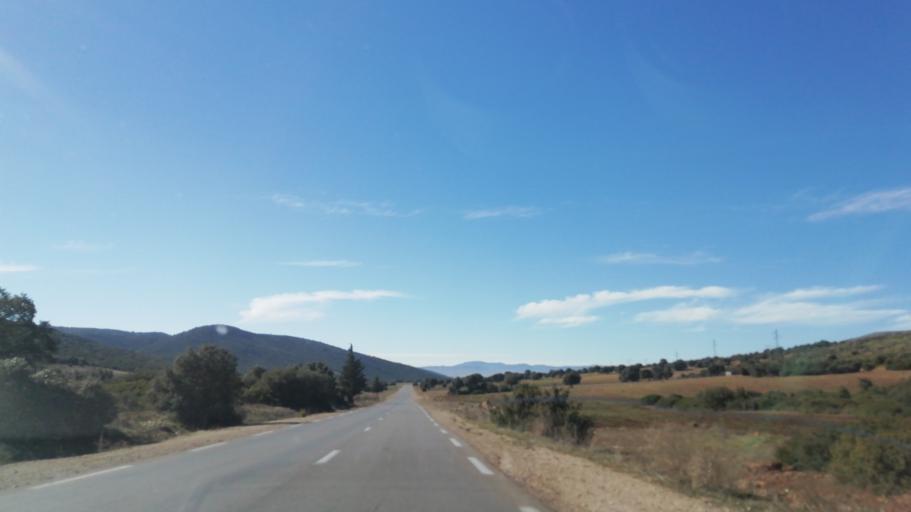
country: DZ
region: Tlemcen
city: Sebdou
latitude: 34.7111
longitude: -1.2110
